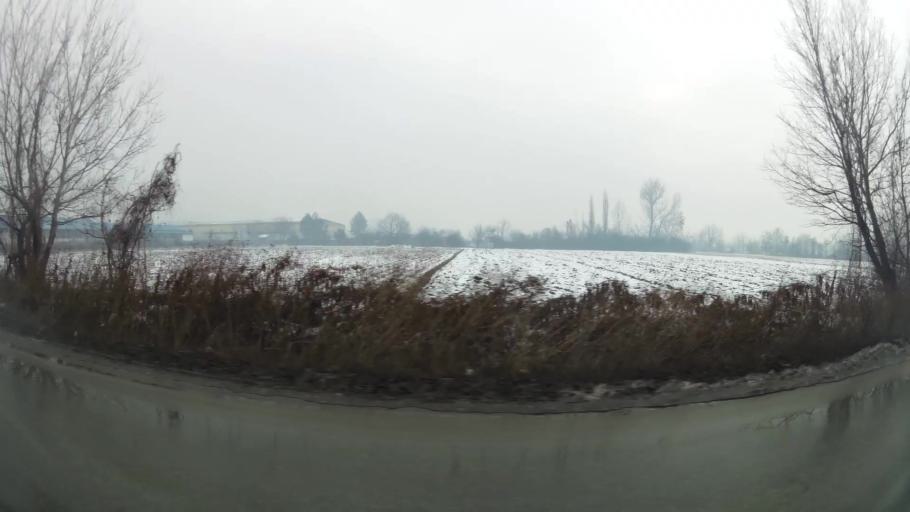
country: MK
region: Ilinden
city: Idrizovo
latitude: 41.9561
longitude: 21.5814
